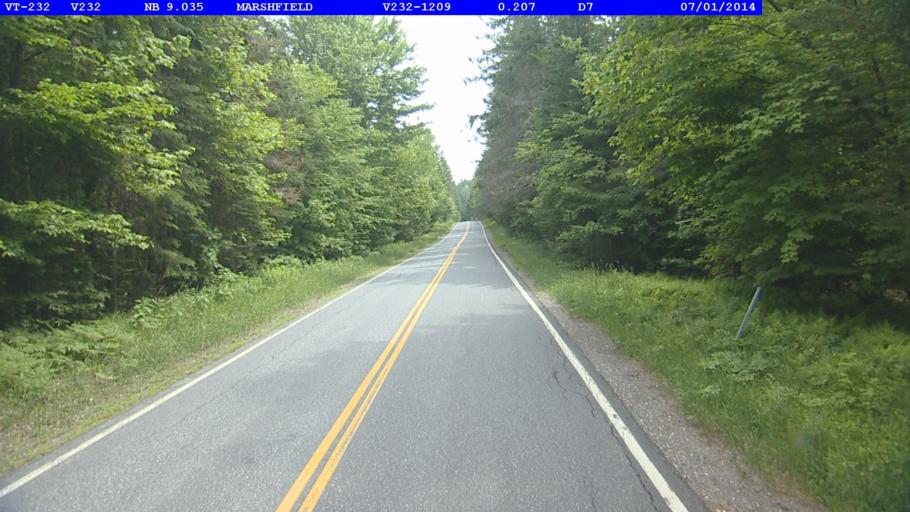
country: US
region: Vermont
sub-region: Caledonia County
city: Hardwick
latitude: 44.3198
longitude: -72.2930
